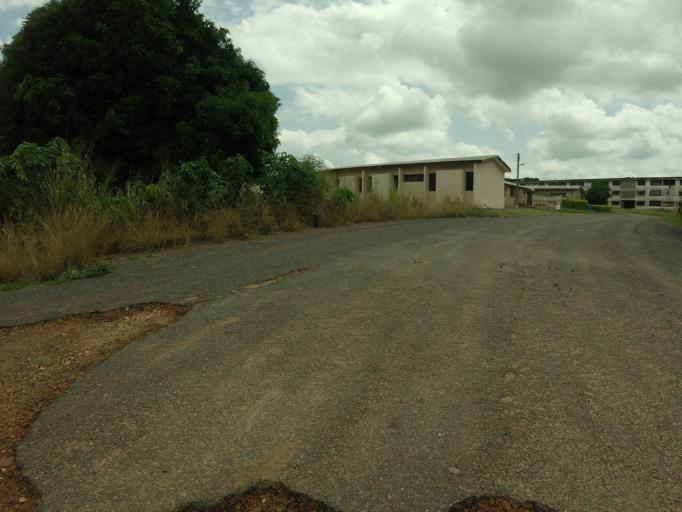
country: GH
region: Volta
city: Ho
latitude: 6.5964
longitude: 0.4841
